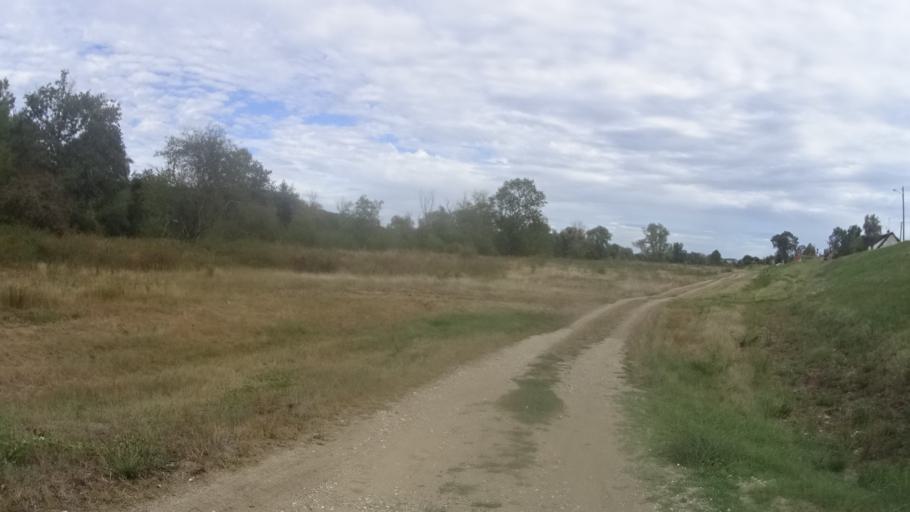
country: FR
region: Centre
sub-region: Departement du Cher
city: Cuffy
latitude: 46.9625
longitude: 3.0683
